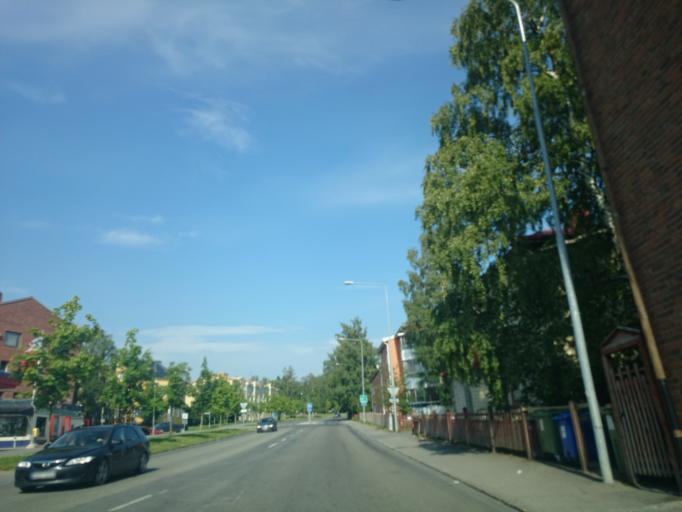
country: SE
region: Jaemtland
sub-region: OEstersunds Kommun
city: Ostersund
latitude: 63.1728
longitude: 14.6426
